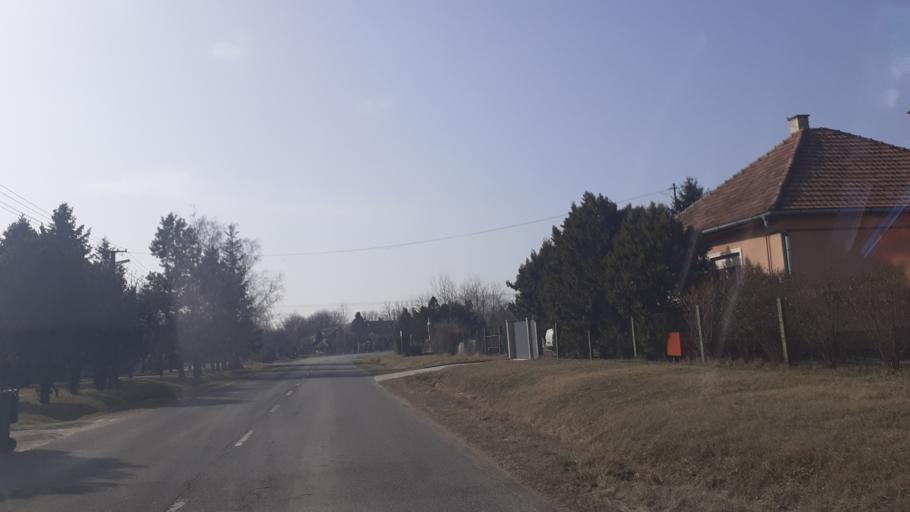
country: HU
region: Pest
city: Orkeny
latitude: 47.1255
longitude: 19.4256
